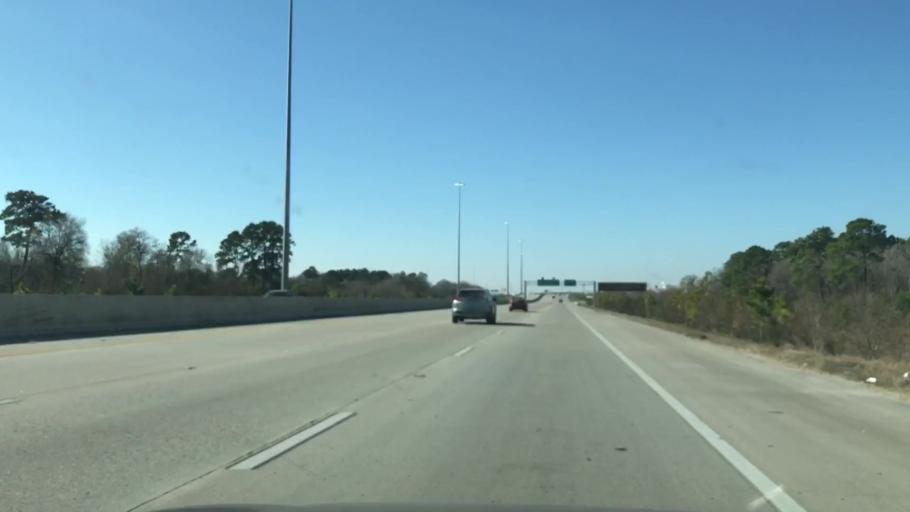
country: US
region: Texas
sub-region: Harris County
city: Jacinto City
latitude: 29.7888
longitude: -95.2402
